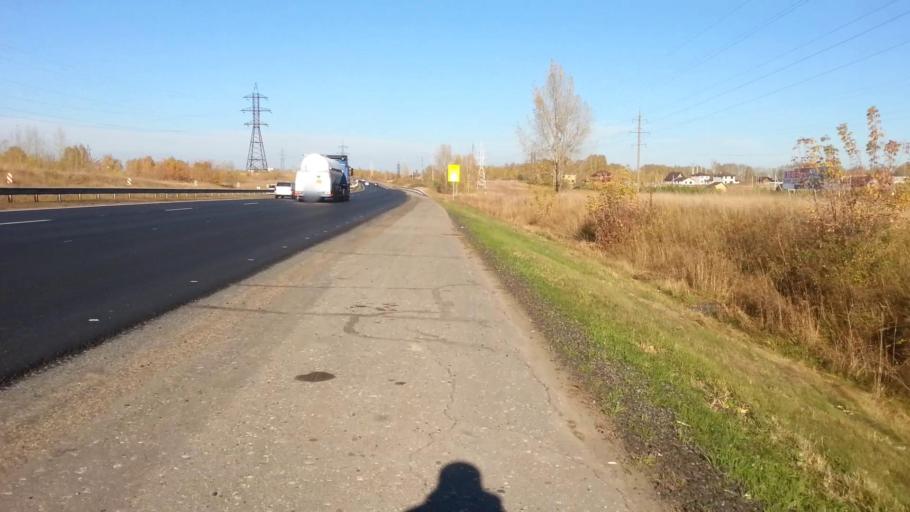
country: RU
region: Altai Krai
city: Sannikovo
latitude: 53.3439
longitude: 83.9413
